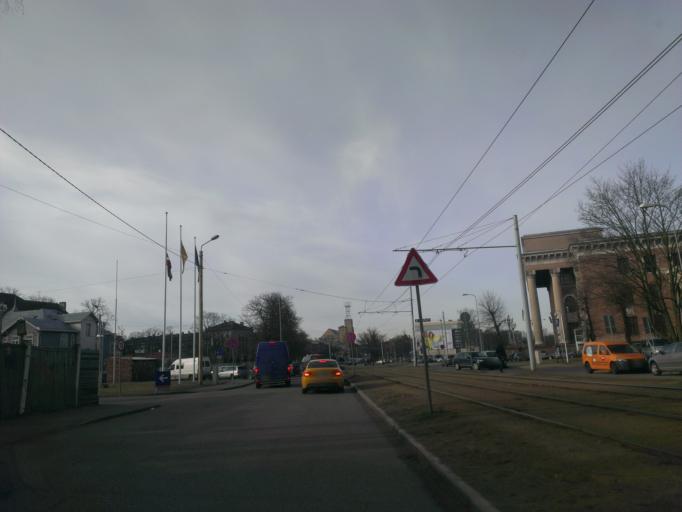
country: LV
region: Riga
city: Jaunciems
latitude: 56.9747
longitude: 24.1678
